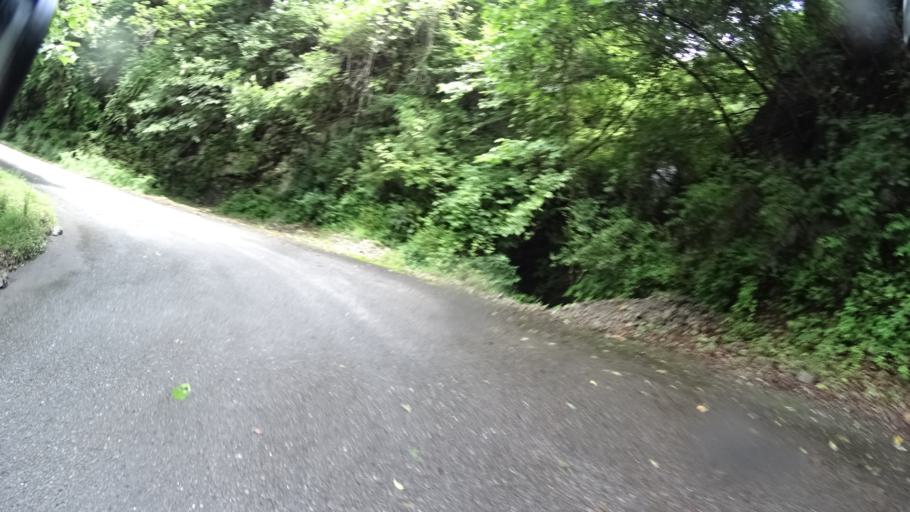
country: JP
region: Saitama
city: Chichibu
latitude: 35.8912
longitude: 139.1358
